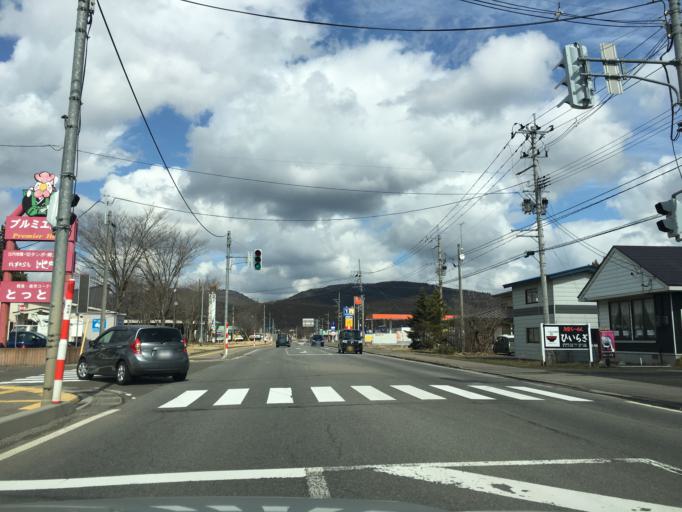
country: JP
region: Akita
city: Odate
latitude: 40.2188
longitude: 140.5857
